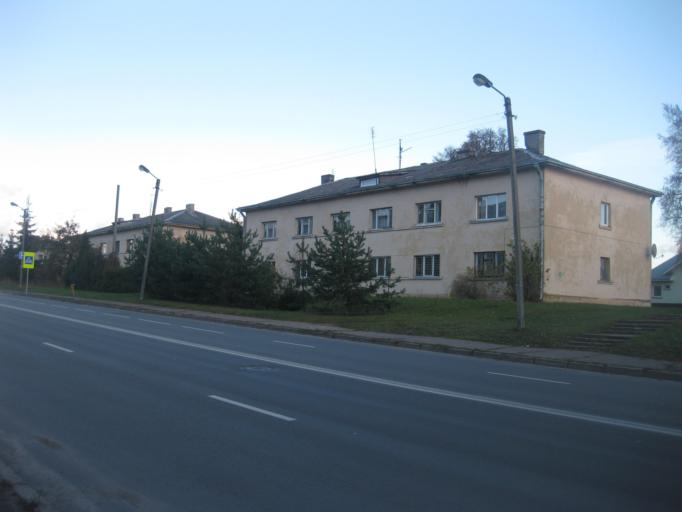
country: LT
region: Kauno apskritis
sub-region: Kaunas
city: Silainiai
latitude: 54.9257
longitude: 23.9038
